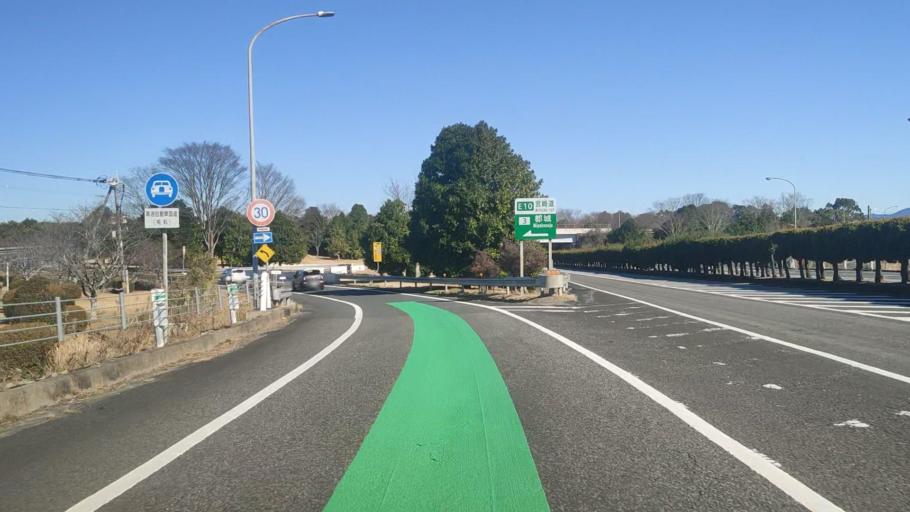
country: JP
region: Miyazaki
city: Miyakonojo
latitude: 31.7807
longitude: 131.1093
